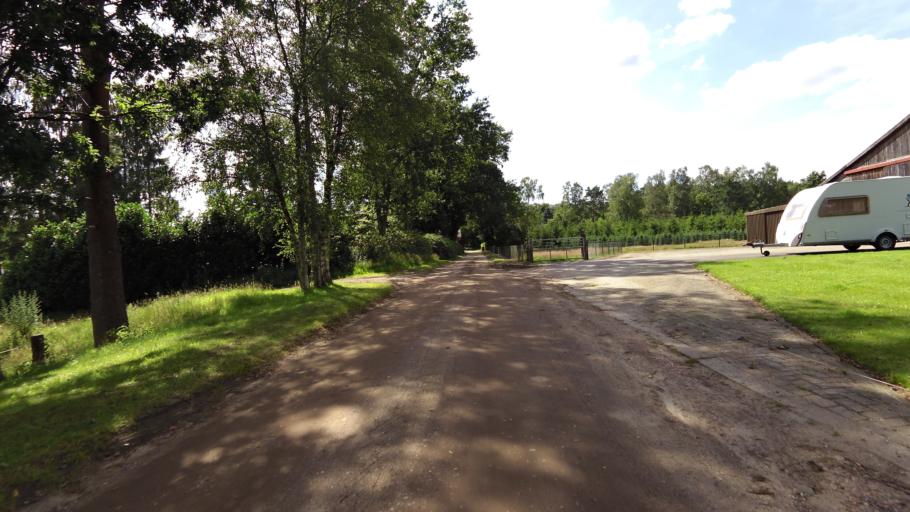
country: NL
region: Gelderland
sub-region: Gemeente Epe
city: Vaassen
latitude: 52.2729
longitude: 5.9259
